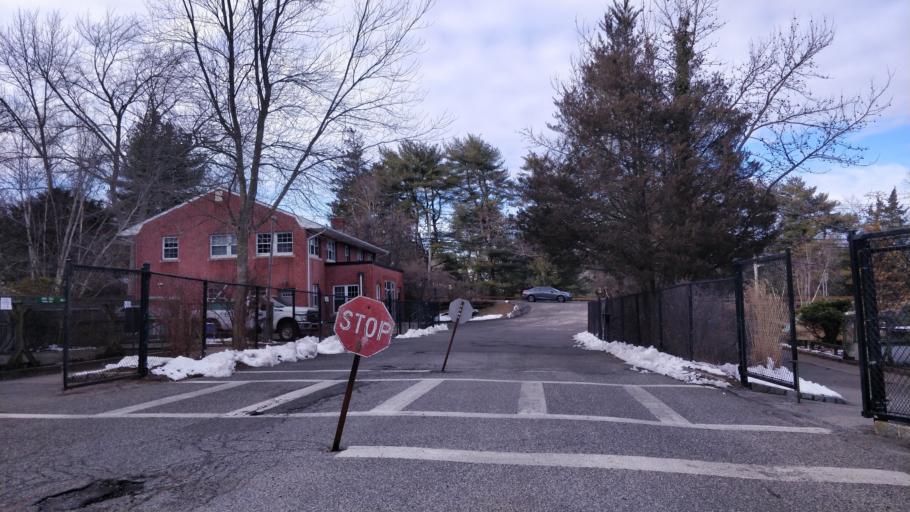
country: US
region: New York
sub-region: Nassau County
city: Laurel Hollow
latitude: 40.8570
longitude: -73.4644
